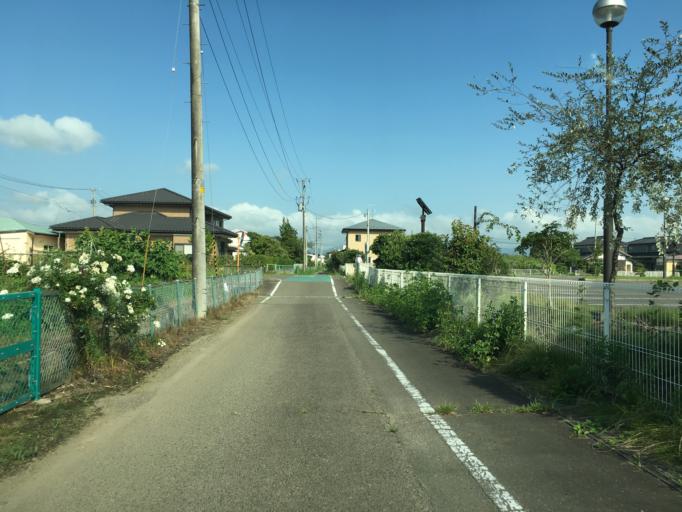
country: JP
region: Miyagi
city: Marumori
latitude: 37.9253
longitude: 140.7670
